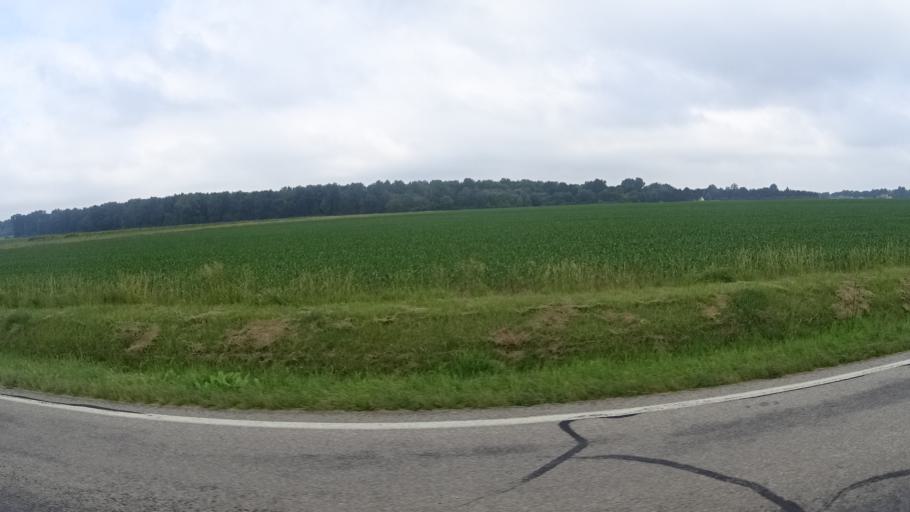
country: US
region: Ohio
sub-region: Huron County
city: Wakeman
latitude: 41.2937
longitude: -82.4925
